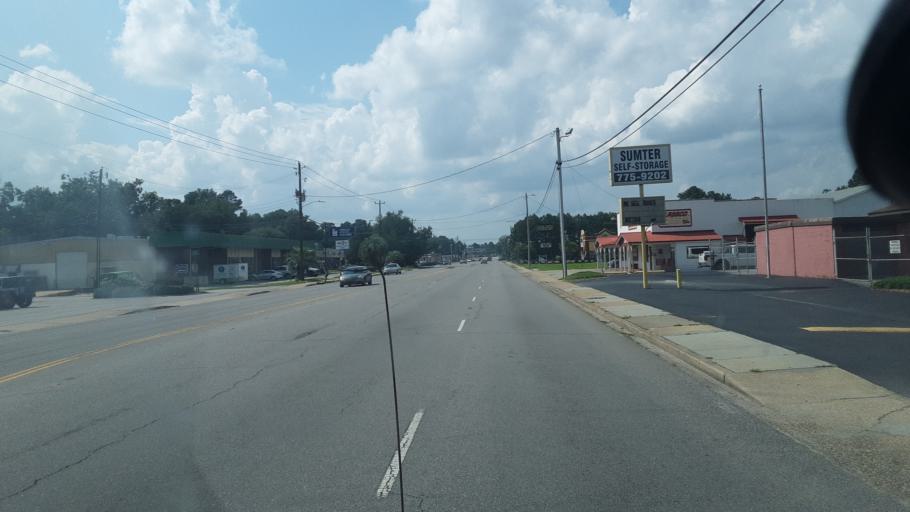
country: US
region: South Carolina
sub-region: Sumter County
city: Sumter
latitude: 33.9415
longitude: -80.3667
